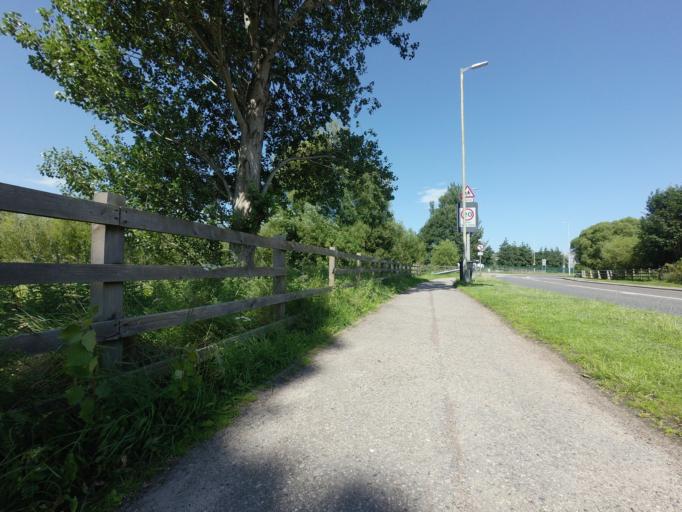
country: GB
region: Scotland
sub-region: Highland
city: Dingwall
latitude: 57.5996
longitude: -4.4325
